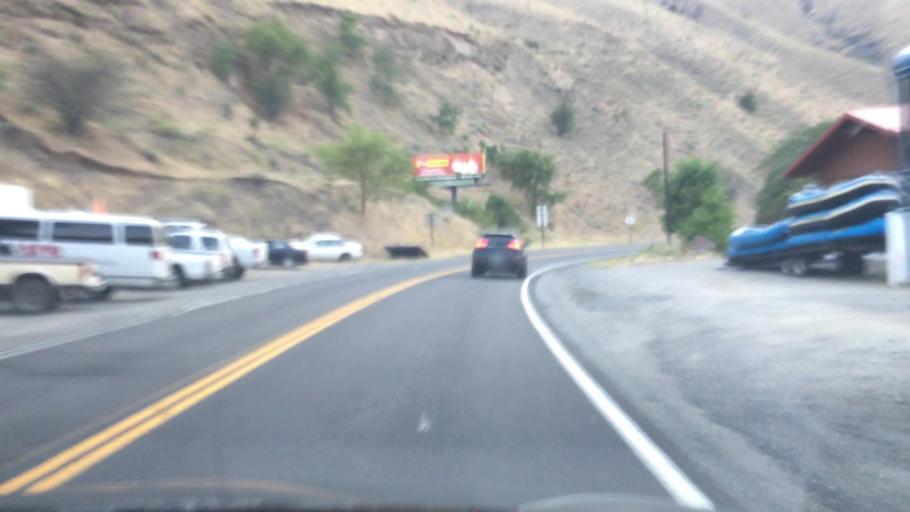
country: US
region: Idaho
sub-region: Idaho County
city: Grangeville
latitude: 45.4314
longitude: -116.3159
